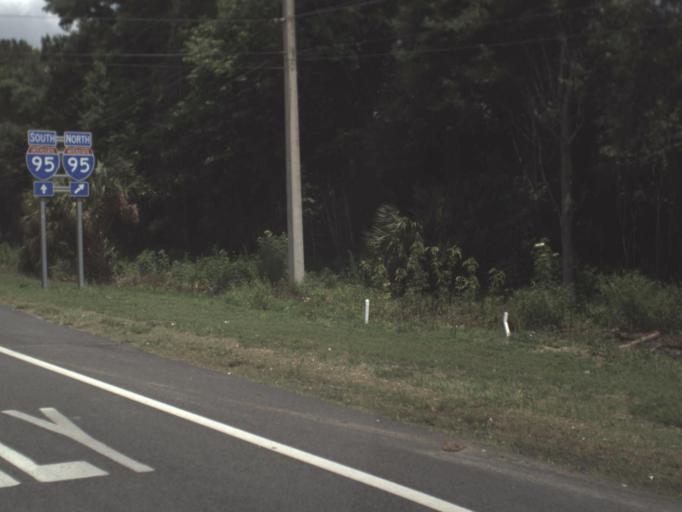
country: US
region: Florida
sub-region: Saint Johns County
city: Fruit Cove
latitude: 30.1826
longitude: -81.5558
